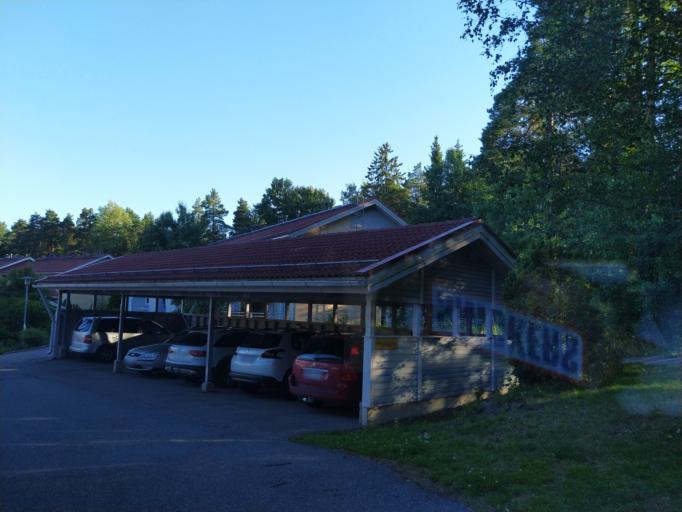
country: FI
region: Varsinais-Suomi
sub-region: Turku
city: Kaarina
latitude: 60.4467
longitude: 22.3346
